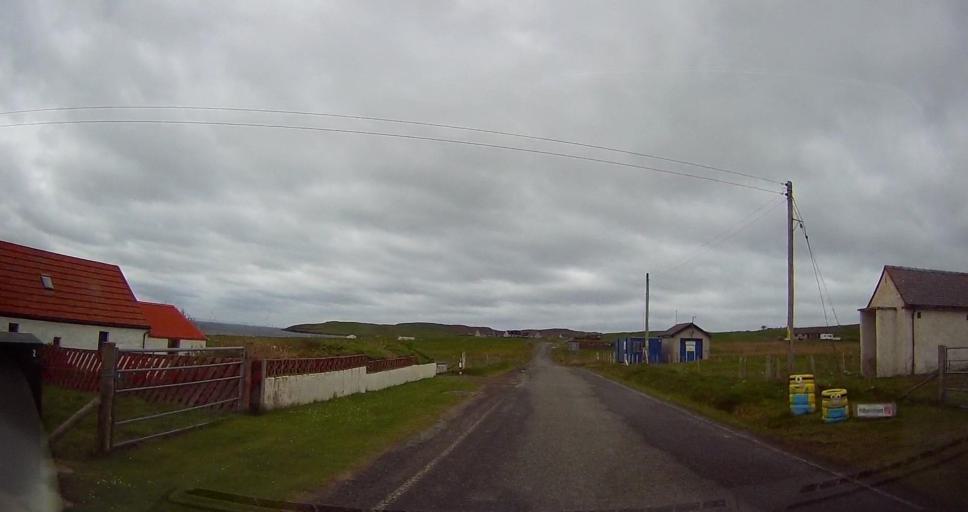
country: GB
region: Scotland
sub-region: Shetland Islands
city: Lerwick
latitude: 60.4829
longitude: -1.4741
